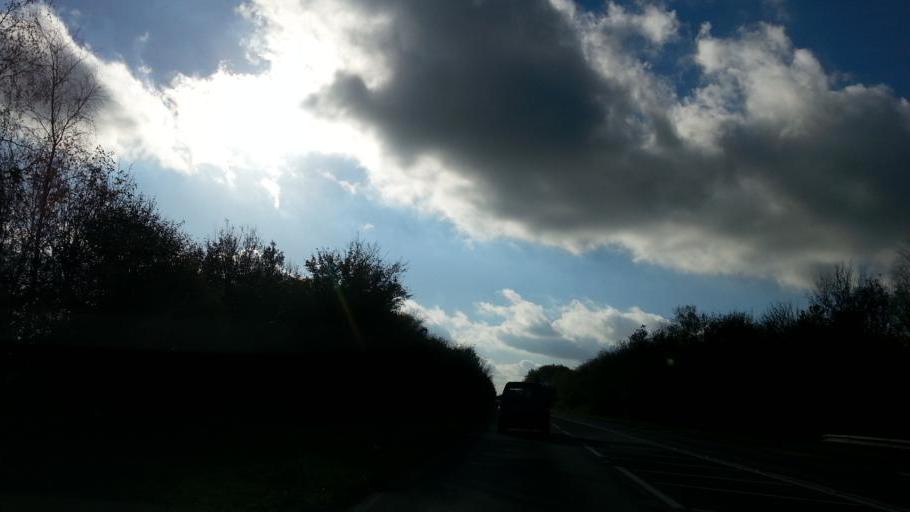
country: GB
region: England
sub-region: Norfolk
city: Harleston
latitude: 52.3923
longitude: 1.2762
